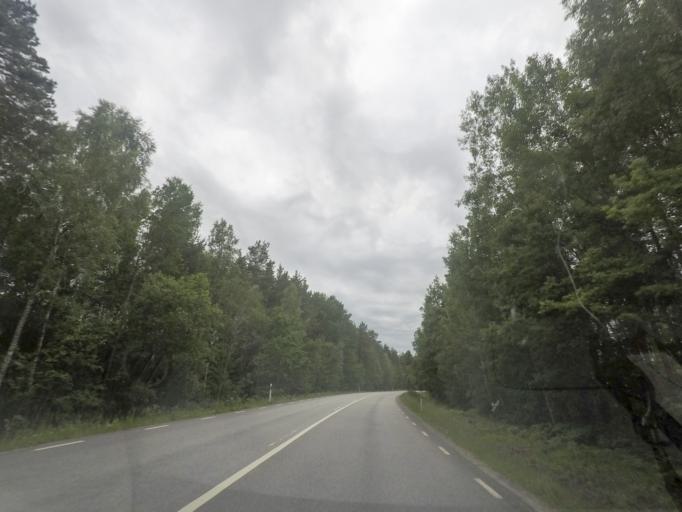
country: SE
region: Vaestmanland
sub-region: Arboga Kommun
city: Arboga
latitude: 59.4121
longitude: 15.7771
